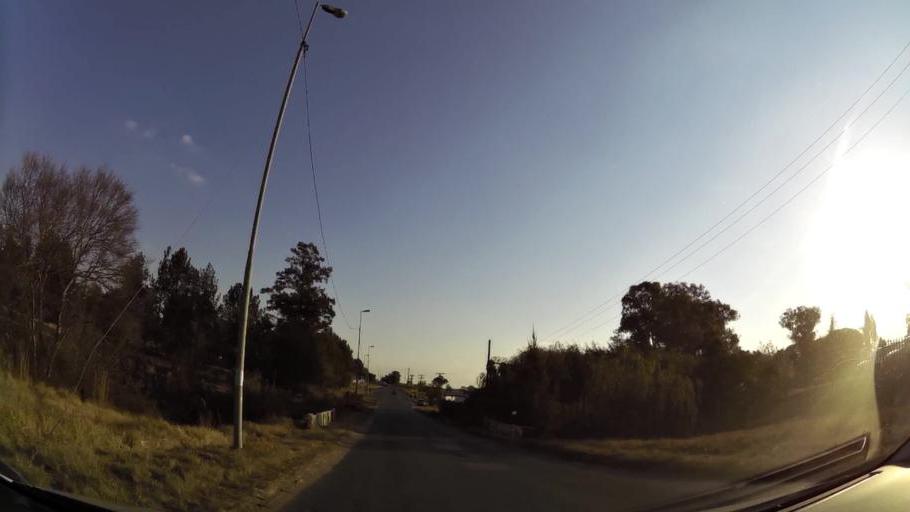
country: ZA
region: Gauteng
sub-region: City of Johannesburg Metropolitan Municipality
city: Midrand
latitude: -26.0306
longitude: 28.1410
